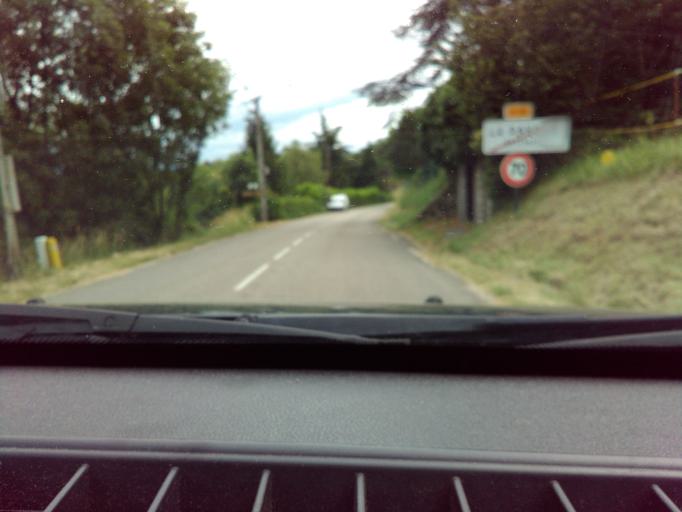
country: FR
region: Rhone-Alpes
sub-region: Departement de la Savoie
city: Barberaz
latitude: 45.5466
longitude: 5.9473
